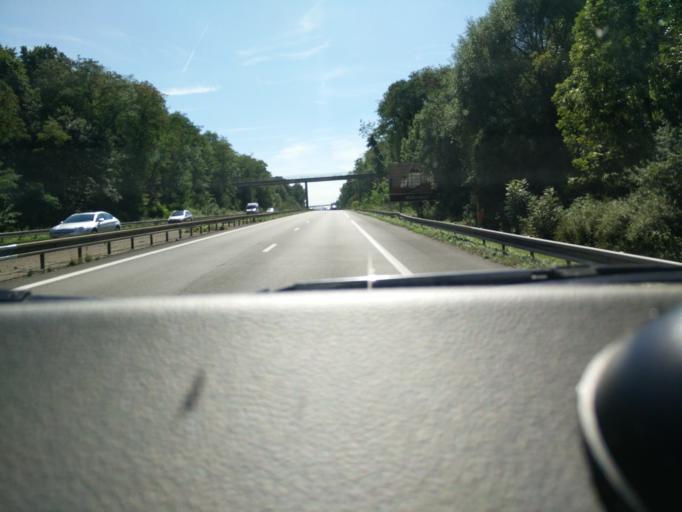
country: FR
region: Lorraine
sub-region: Departement de la Moselle
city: Entrange
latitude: 49.3882
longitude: 6.1085
